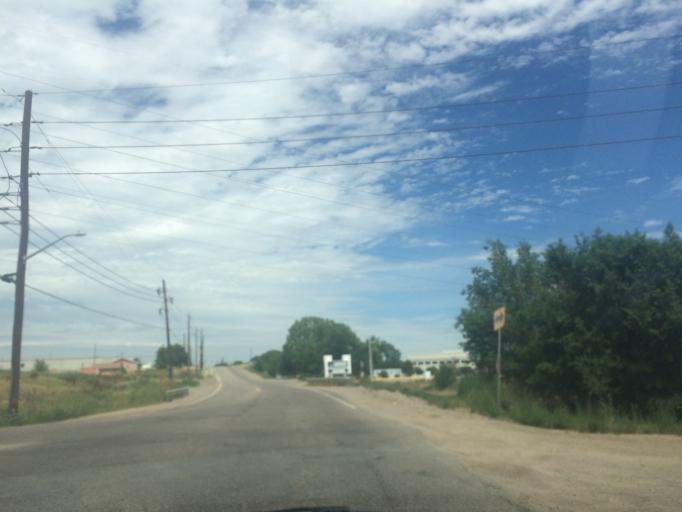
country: US
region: Colorado
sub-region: Adams County
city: Welby
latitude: 39.8125
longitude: -104.9593
